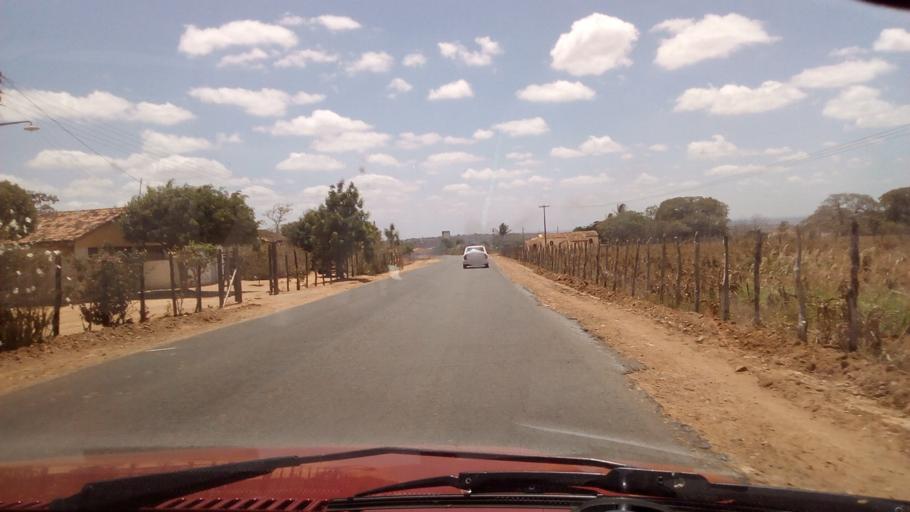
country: BR
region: Paraiba
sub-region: Cacimba De Dentro
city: Cacimba de Dentro
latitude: -6.6049
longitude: -35.8093
